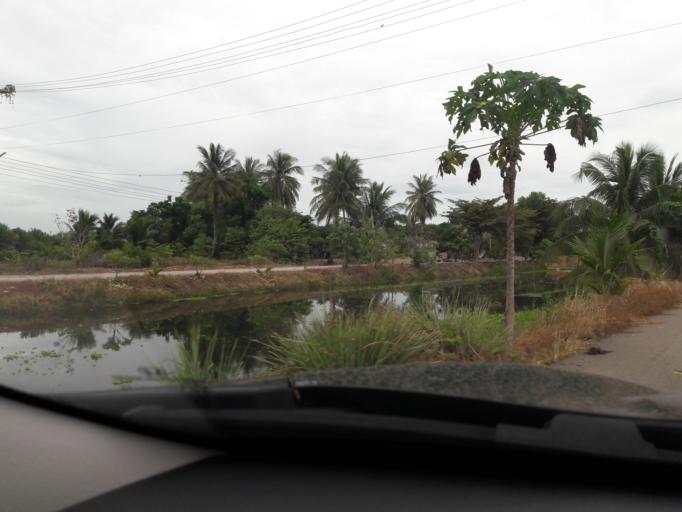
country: TH
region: Ratchaburi
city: Damnoen Saduak
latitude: 13.6043
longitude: 99.9731
